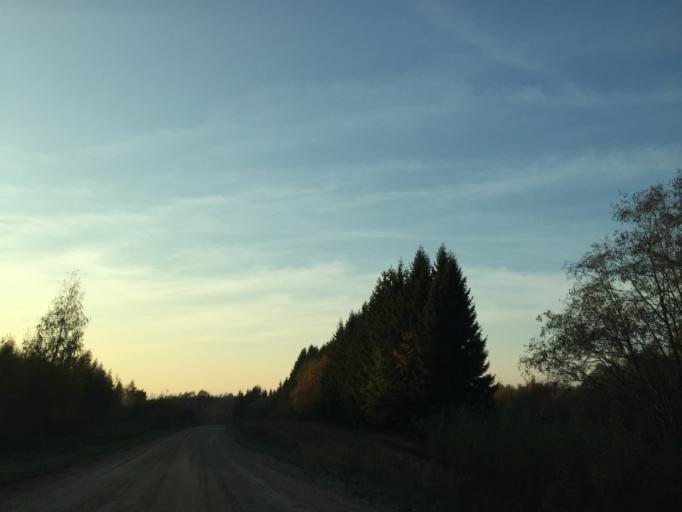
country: LV
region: Vainode
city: Vainode
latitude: 56.4892
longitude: 21.7821
